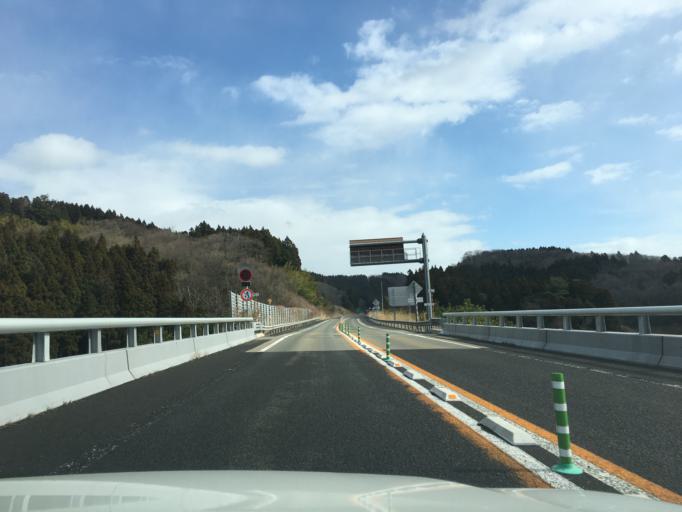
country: JP
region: Akita
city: Akita Shi
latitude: 39.5515
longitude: 140.0765
